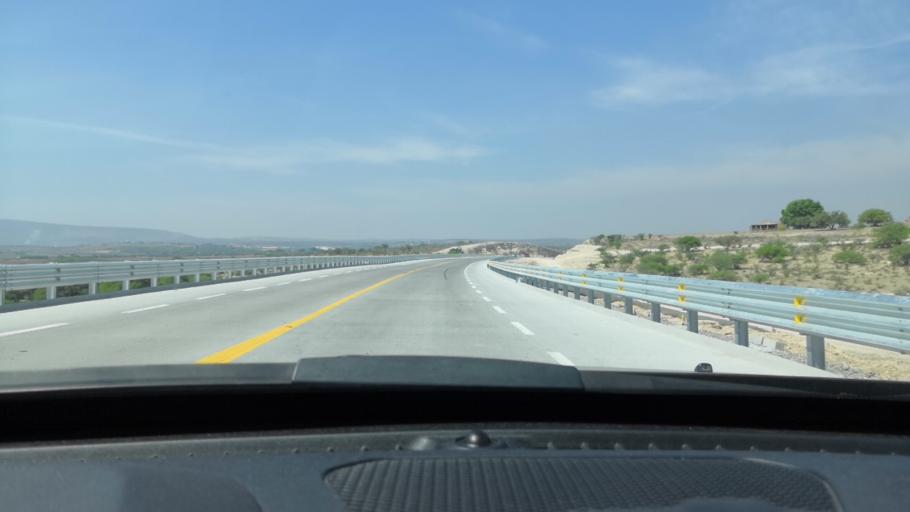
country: MX
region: Guanajuato
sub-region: Purisima del Rincon
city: Potrerillos (Guanajal)
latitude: 21.0839
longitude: -101.8335
